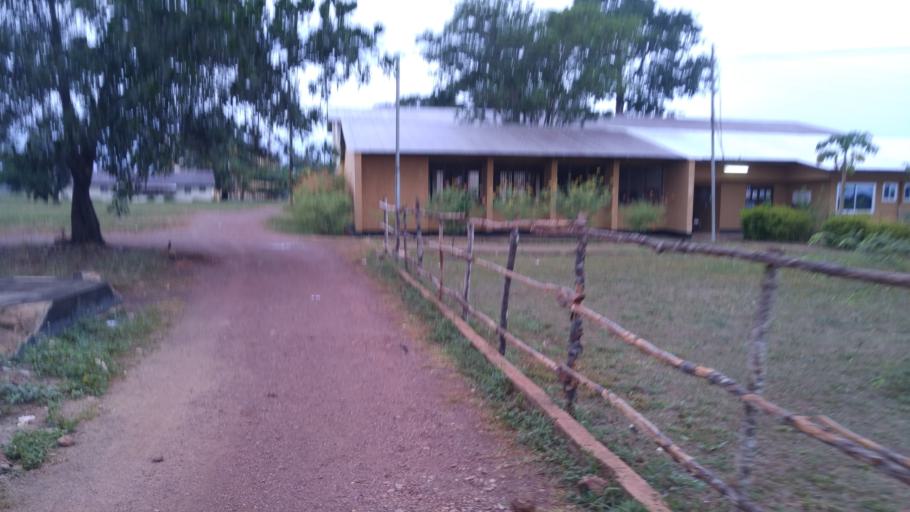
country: SL
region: Southern Province
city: Largo
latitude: 8.1154
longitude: -12.0685
